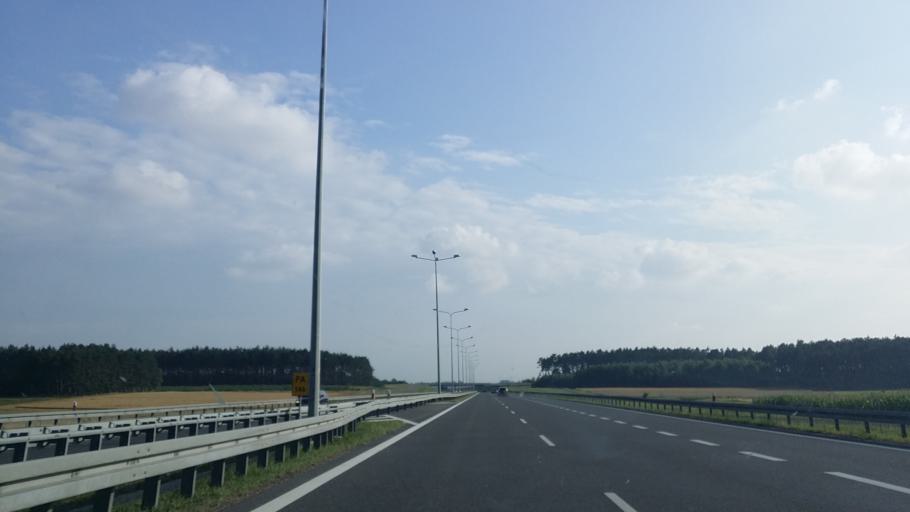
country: PL
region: Lubusz
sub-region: Powiat swiebodzinski
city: Swiebodzin
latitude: 52.3179
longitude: 15.5488
